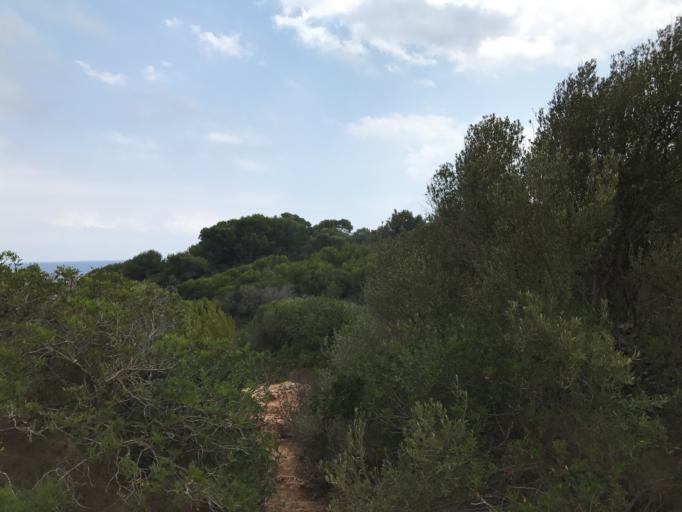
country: ES
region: Balearic Islands
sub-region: Illes Balears
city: Sant Llorenc des Cardassar
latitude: 39.5331
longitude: 3.3316
